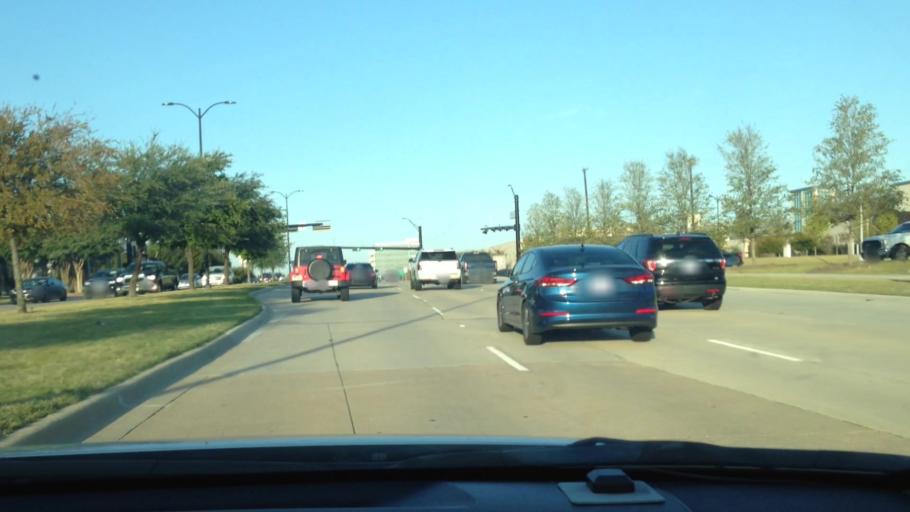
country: US
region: Texas
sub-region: Collin County
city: Frisco
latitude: 33.1068
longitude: -96.8250
